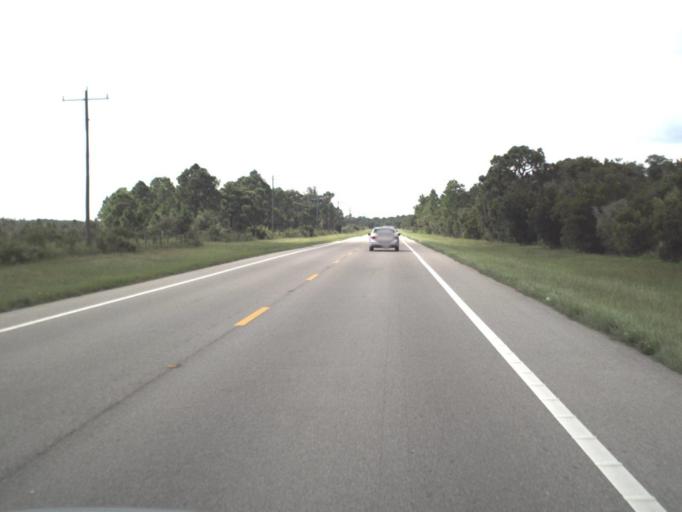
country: US
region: Florida
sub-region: Hillsborough County
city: Wimauma
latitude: 27.4689
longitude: -82.1977
